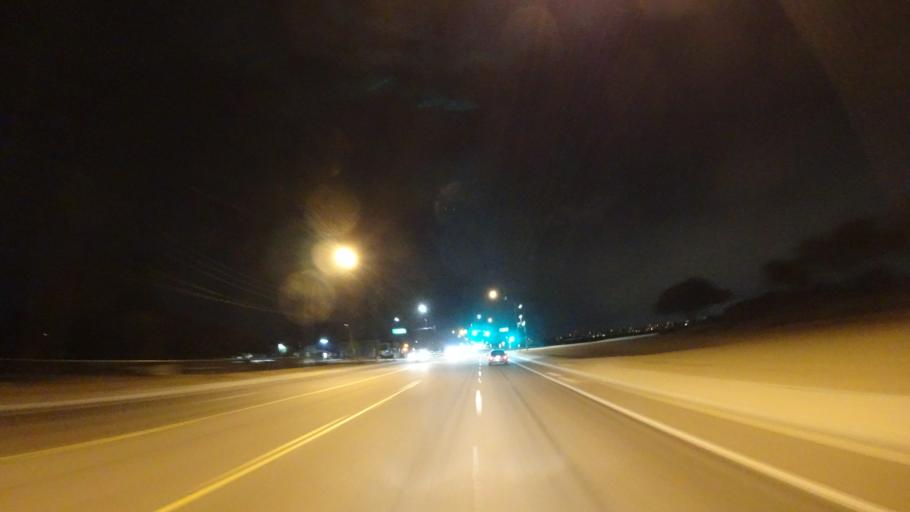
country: US
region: Arizona
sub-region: Maricopa County
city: Gilbert
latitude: 33.2632
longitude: -111.7454
